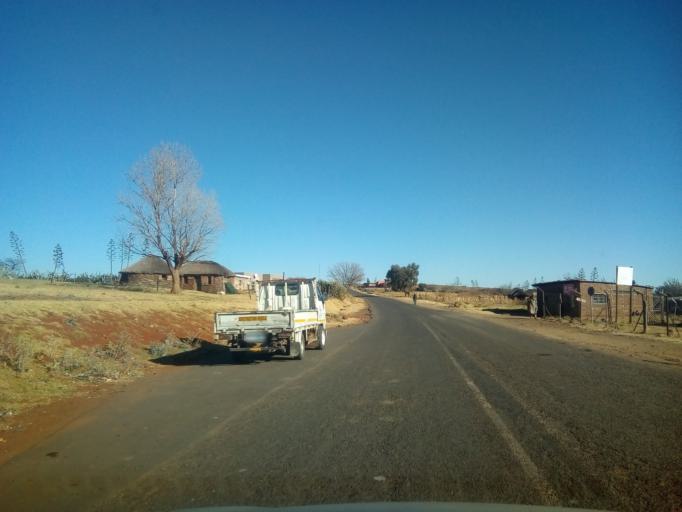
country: LS
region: Berea
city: Teyateyaneng
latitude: -29.2526
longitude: 27.7960
